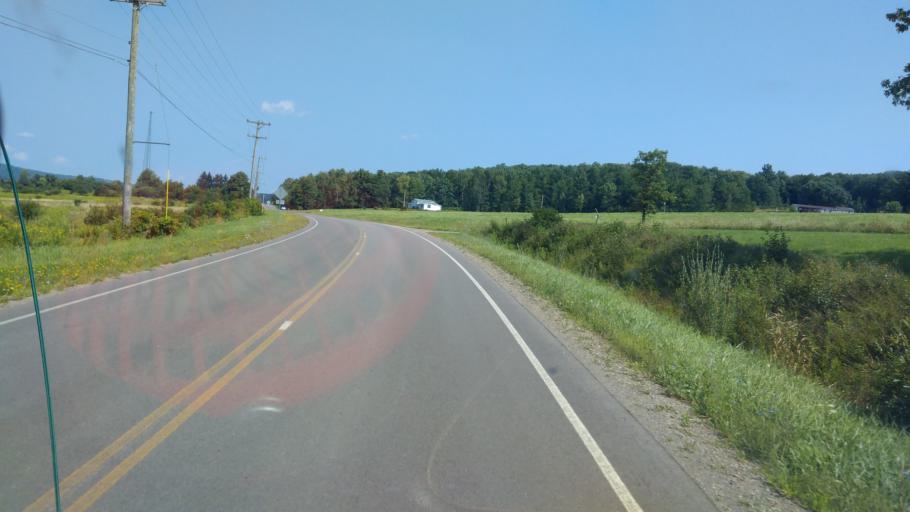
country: US
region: New York
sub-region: Allegany County
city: Belmont
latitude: 42.2897
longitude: -78.0263
